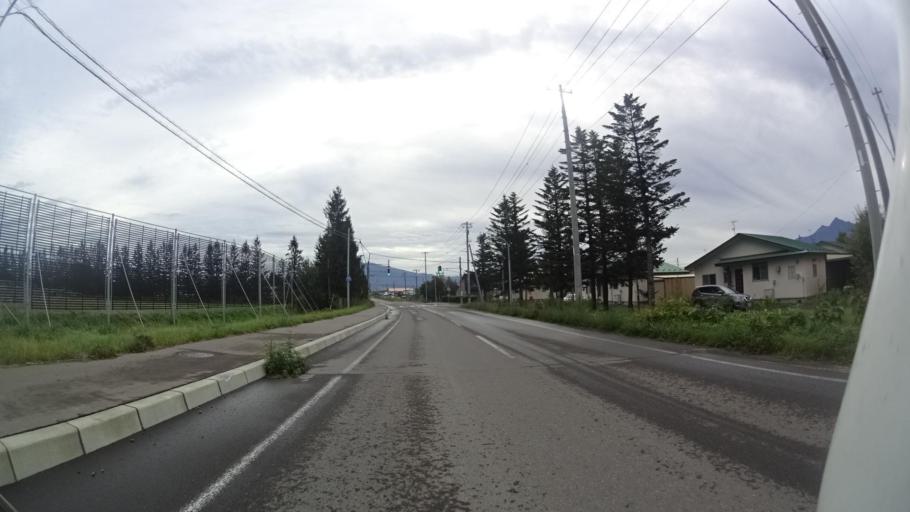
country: JP
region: Hokkaido
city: Abashiri
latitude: 43.8709
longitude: 144.6530
